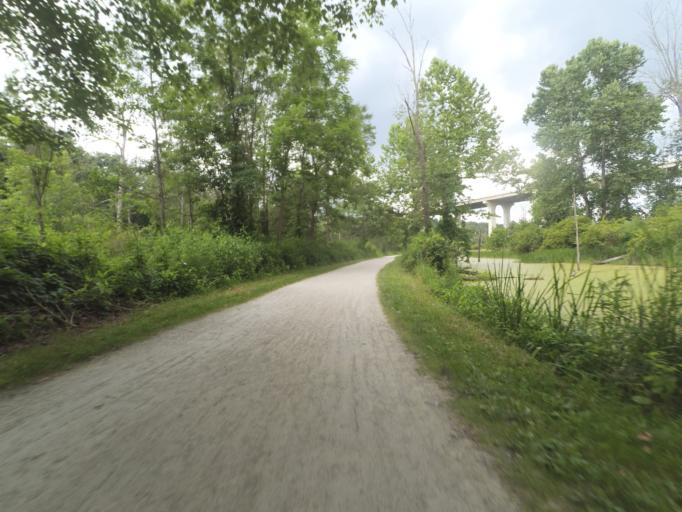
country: US
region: Ohio
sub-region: Summit County
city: Peninsula
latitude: 41.2549
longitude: -81.5517
